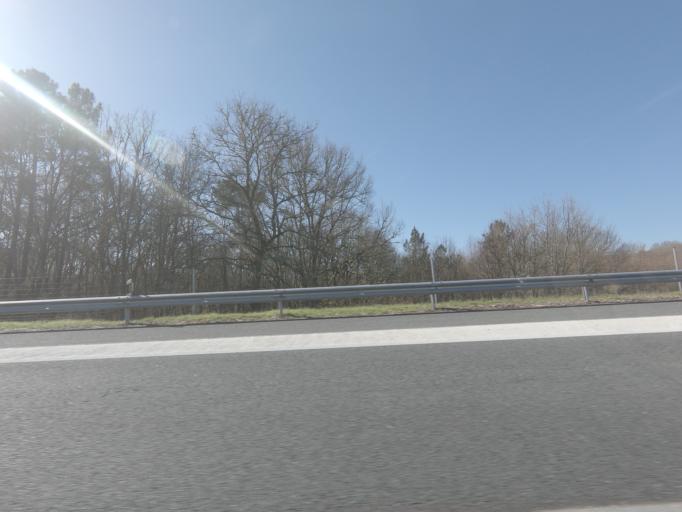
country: ES
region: Galicia
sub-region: Provincia de Ourense
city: Maside
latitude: 42.4026
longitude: -8.0086
